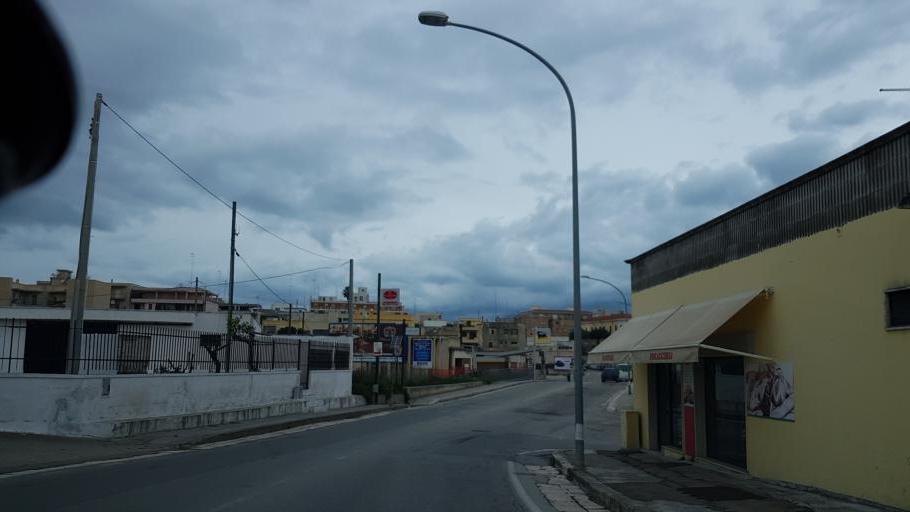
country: IT
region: Apulia
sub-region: Provincia di Brindisi
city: Brindisi
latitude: 40.6302
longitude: 17.9459
